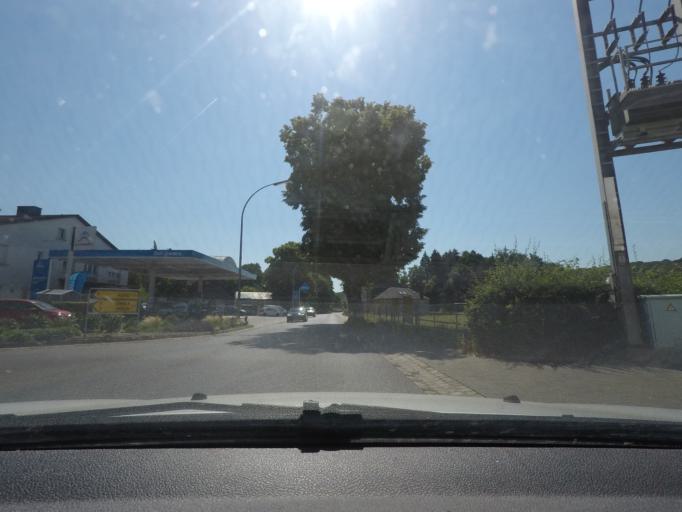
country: LU
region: Diekirch
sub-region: Canton de Redange
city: Redange-sur-Attert
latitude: 49.7658
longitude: 5.8791
